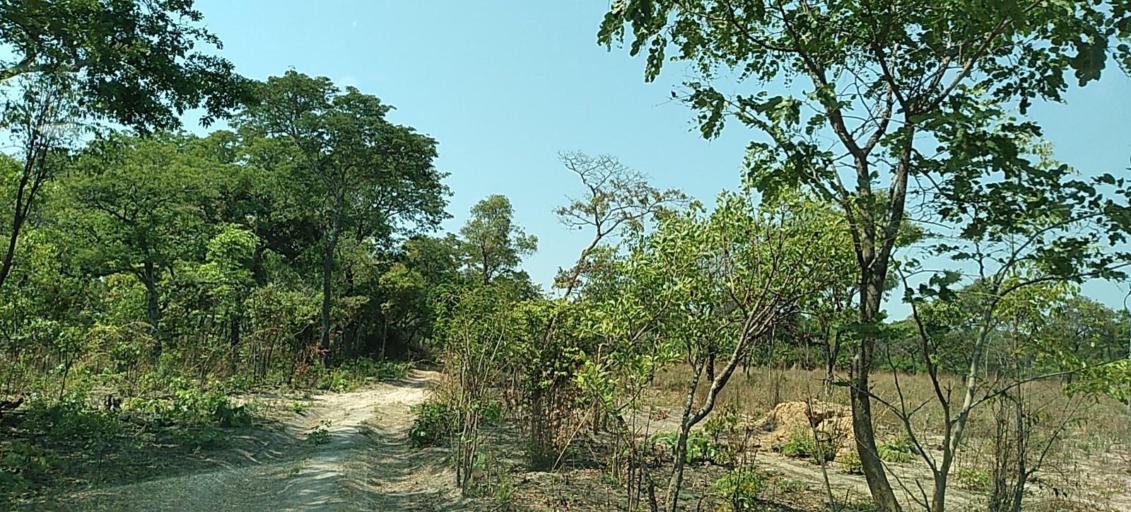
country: ZM
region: Copperbelt
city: Mpongwe
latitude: -13.7875
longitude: 28.0986
